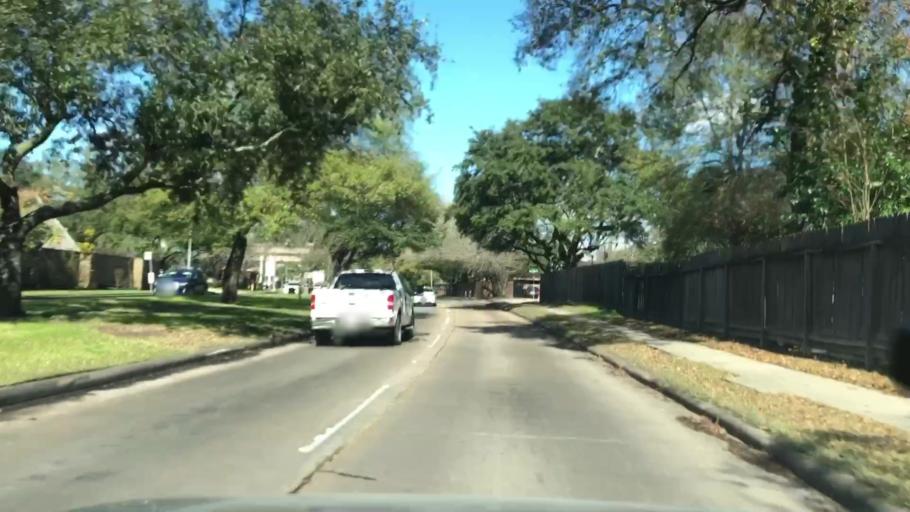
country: US
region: Texas
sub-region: Harris County
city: Bellaire
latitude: 29.6720
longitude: -95.4924
